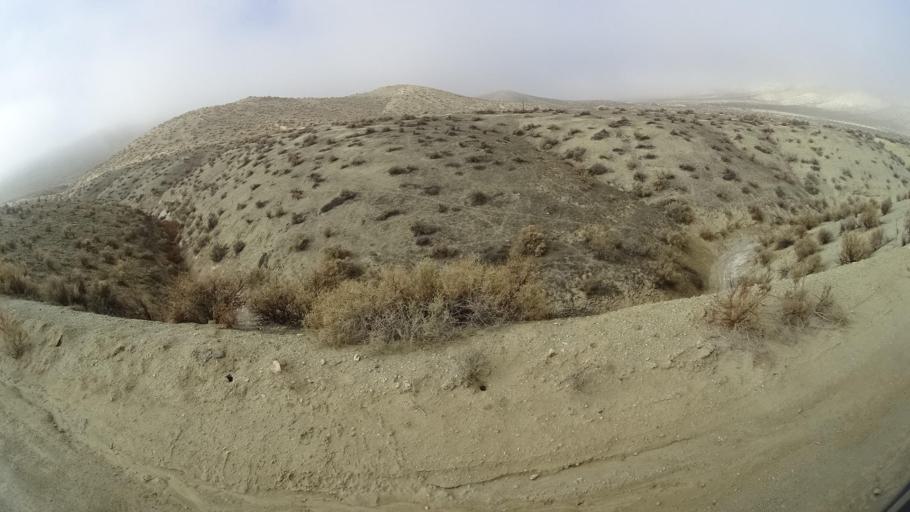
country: US
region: California
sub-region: Kern County
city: Maricopa
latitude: 35.0313
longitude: -119.4400
